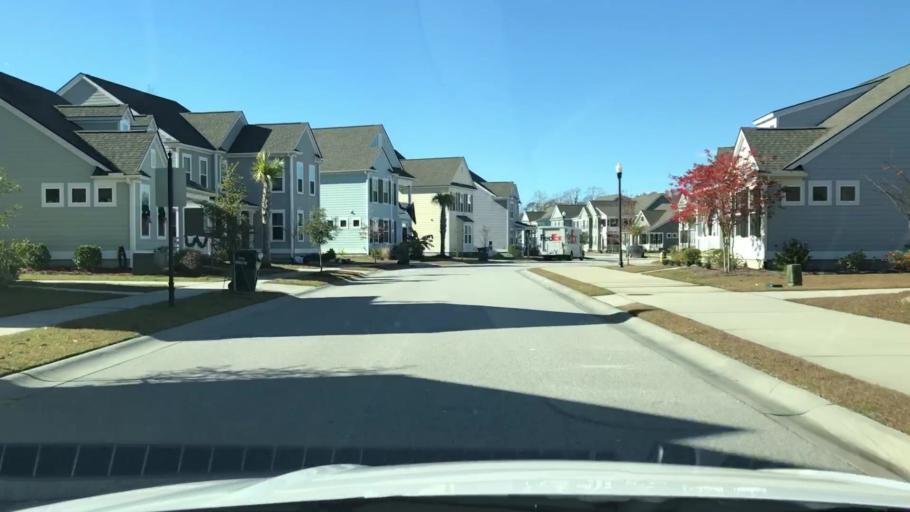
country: US
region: South Carolina
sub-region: Charleston County
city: Shell Point
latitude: 32.8082
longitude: -80.0670
